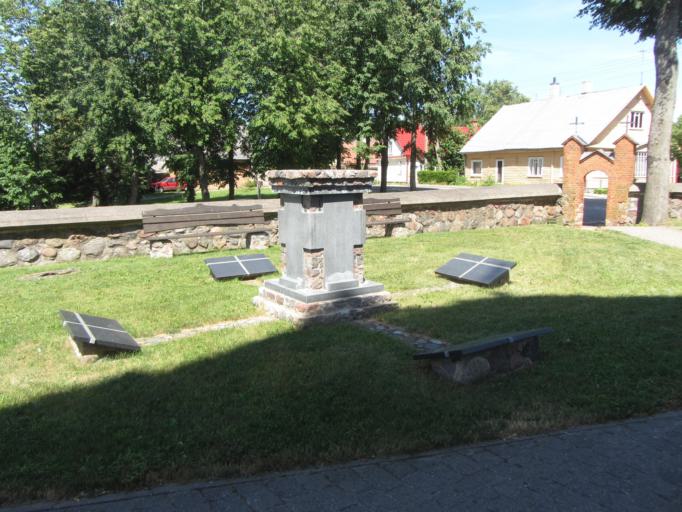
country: LT
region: Alytaus apskritis
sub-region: Alytaus rajonas
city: Daugai
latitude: 54.3599
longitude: 24.3442
